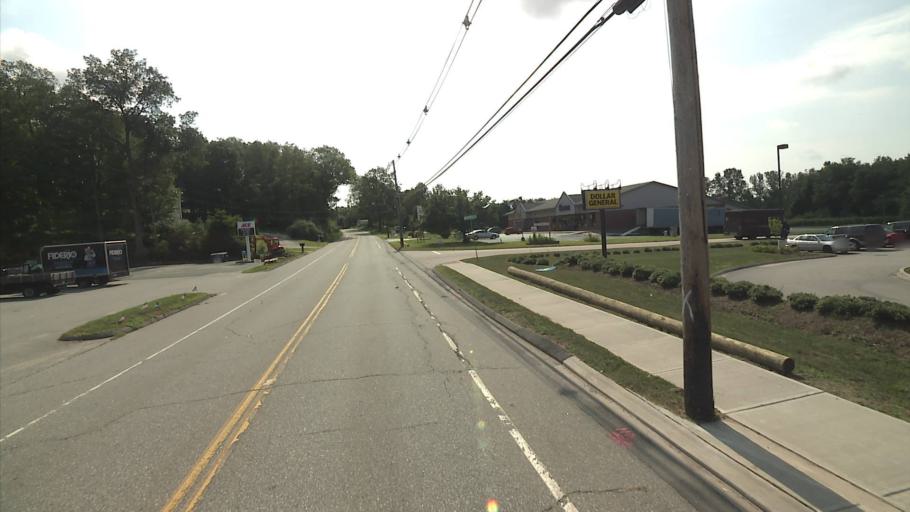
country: US
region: Connecticut
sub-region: New London County
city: Colchester
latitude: 41.5800
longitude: -72.3461
